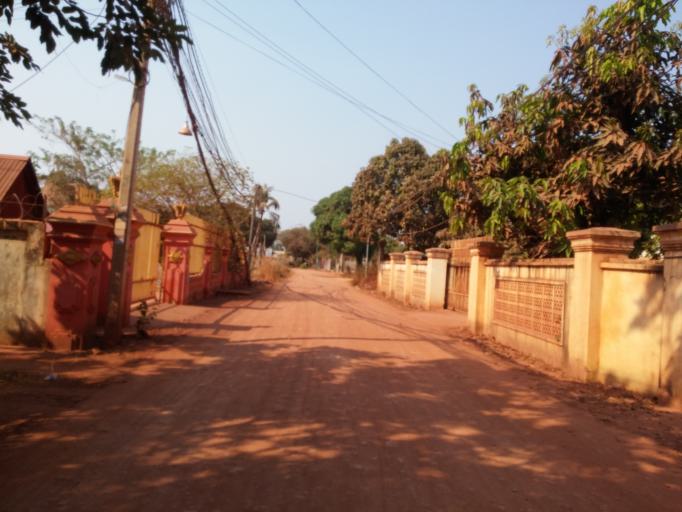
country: KH
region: Siem Reap
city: Siem Reap
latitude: 13.3713
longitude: 103.8478
